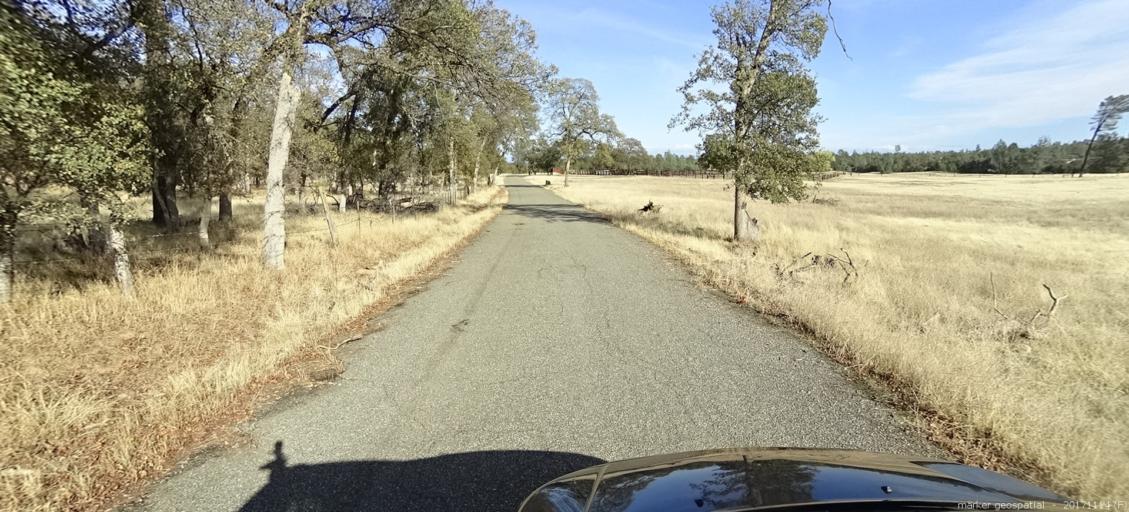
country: US
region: California
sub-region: Shasta County
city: Shasta
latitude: 40.3739
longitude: -122.5608
